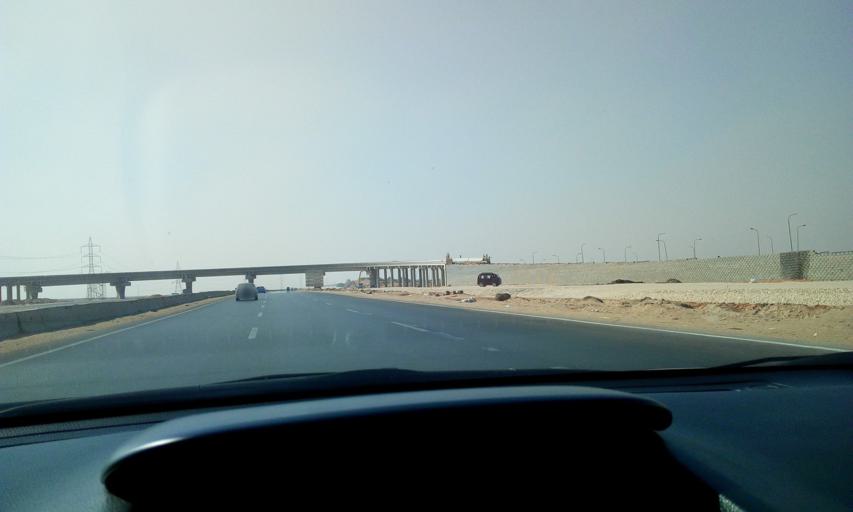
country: EG
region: Al Jizah
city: Madinat Sittah Uktubar
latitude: 29.9290
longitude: 31.0964
